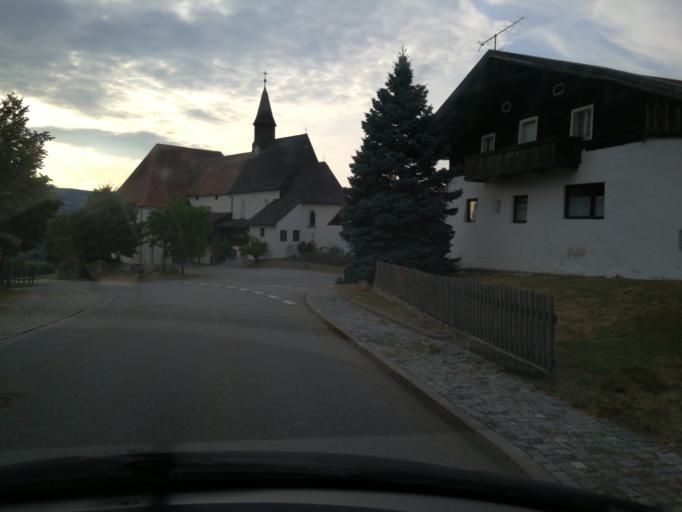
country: DE
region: Bavaria
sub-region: Lower Bavaria
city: Rattiszell
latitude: 49.0348
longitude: 12.6699
